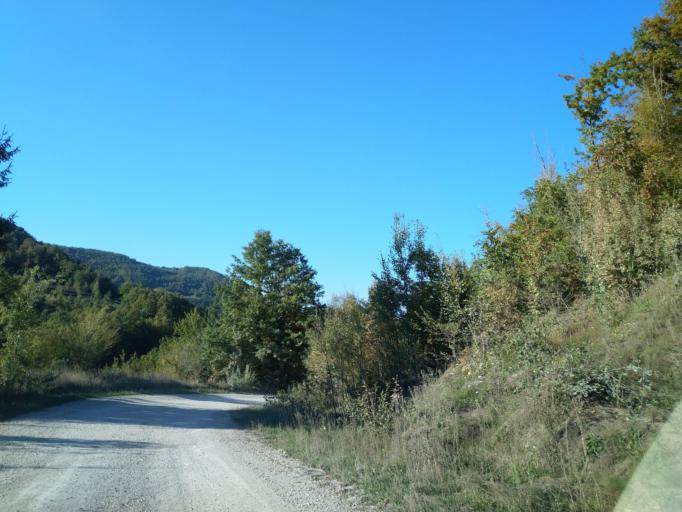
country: RS
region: Central Serbia
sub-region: Moravicki Okrug
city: Ivanjica
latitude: 43.4771
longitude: 20.2383
